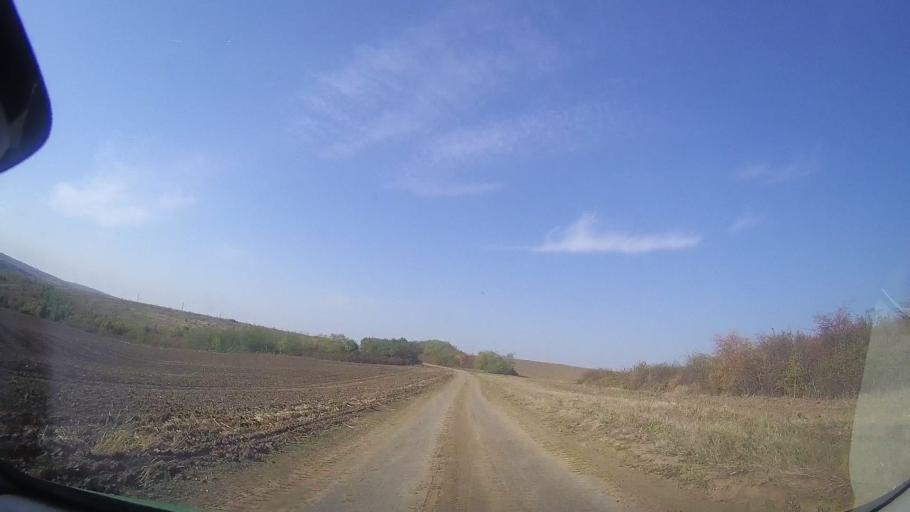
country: RO
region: Timis
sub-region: Oras Recas
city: Recas
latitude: 45.8817
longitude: 21.5360
